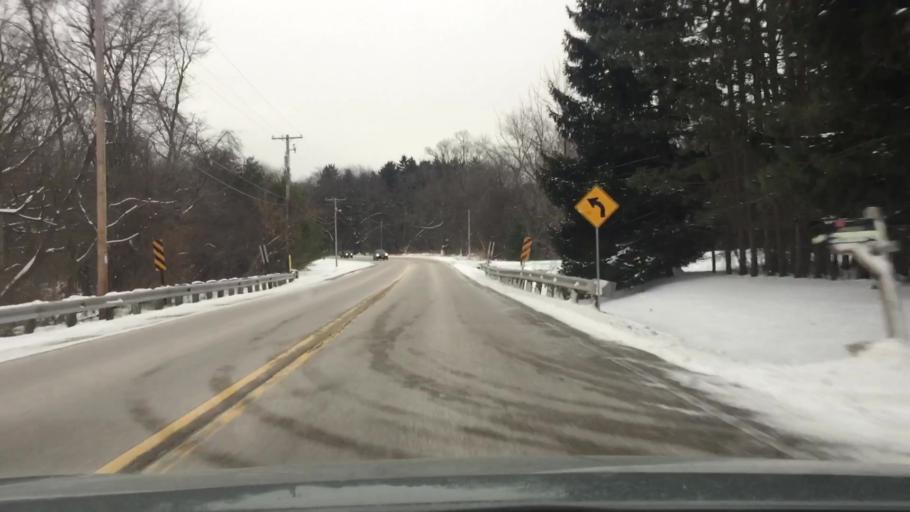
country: US
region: Wisconsin
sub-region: Waukesha County
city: Hartland
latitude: 43.0490
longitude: -88.3165
